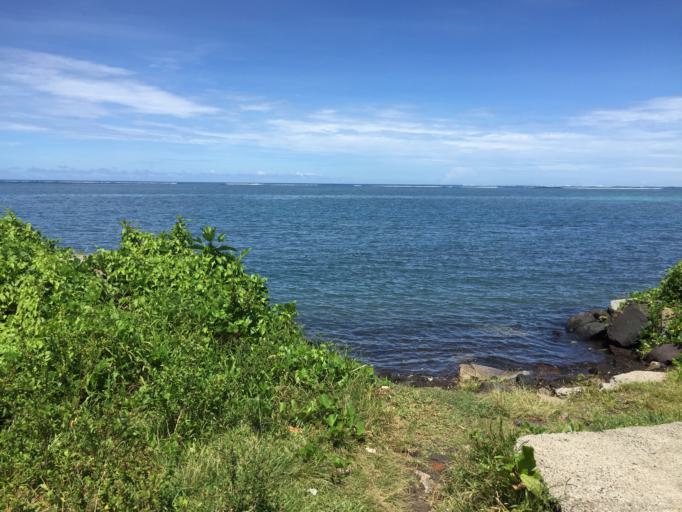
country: WS
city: Lotofaga
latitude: -14.0123
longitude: -171.7805
